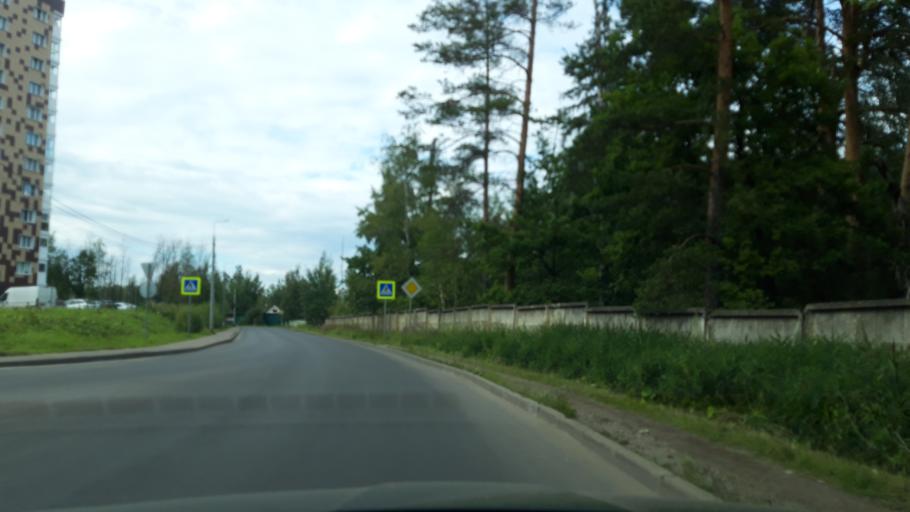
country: RU
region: Moskovskaya
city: Andreyevka
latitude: 55.9813
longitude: 37.1146
